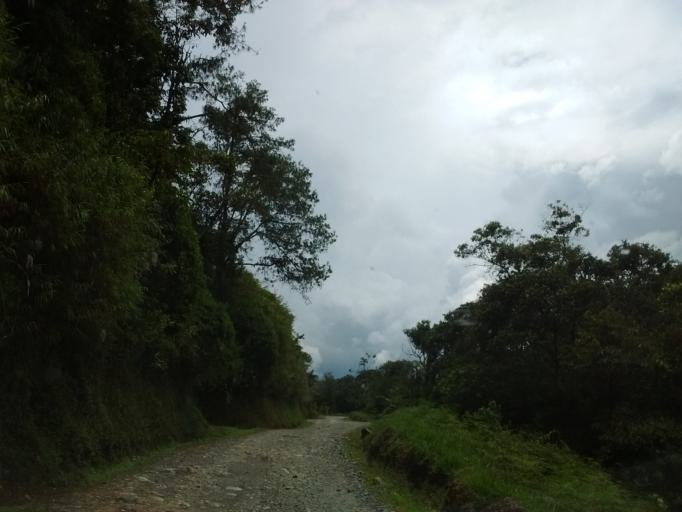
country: CO
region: Cauca
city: Cajibio
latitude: 2.5568
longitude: -76.6355
